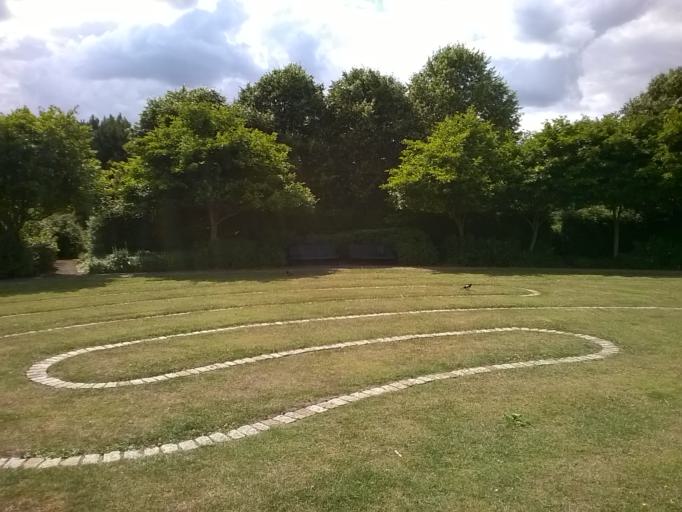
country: GB
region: England
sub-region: Milton Keynes
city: Milton Keynes
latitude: 52.0473
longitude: -0.7474
